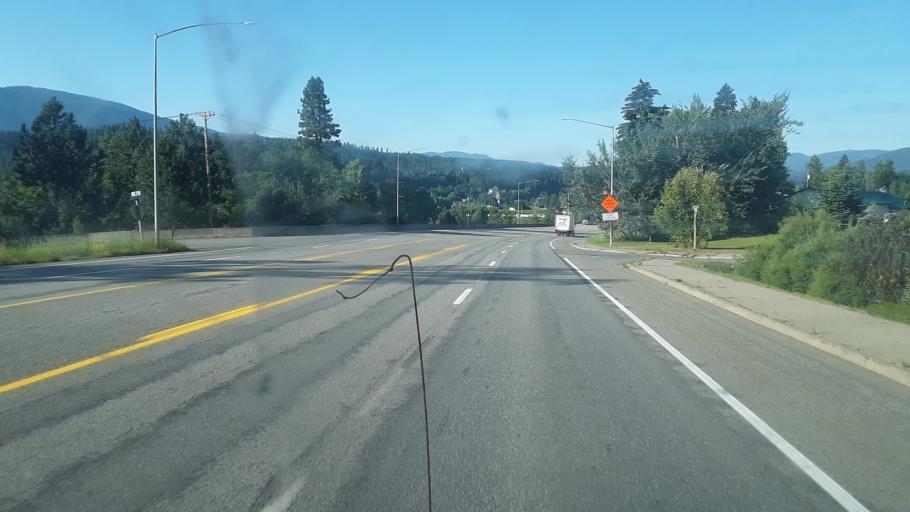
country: US
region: Idaho
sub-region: Boundary County
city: Bonners Ferry
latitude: 48.7062
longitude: -116.3109
